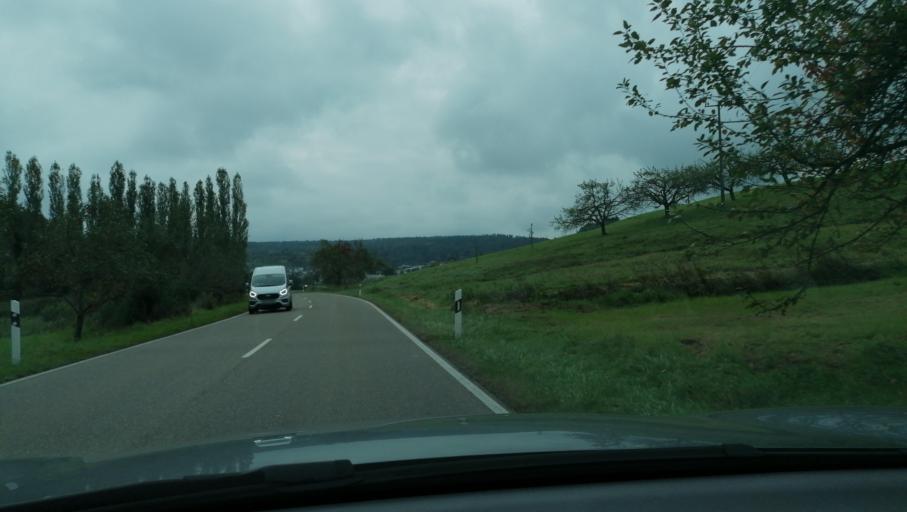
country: DE
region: Baden-Wuerttemberg
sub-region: Regierungsbezirk Stuttgart
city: Winnenden
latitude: 48.8524
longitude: 9.4427
